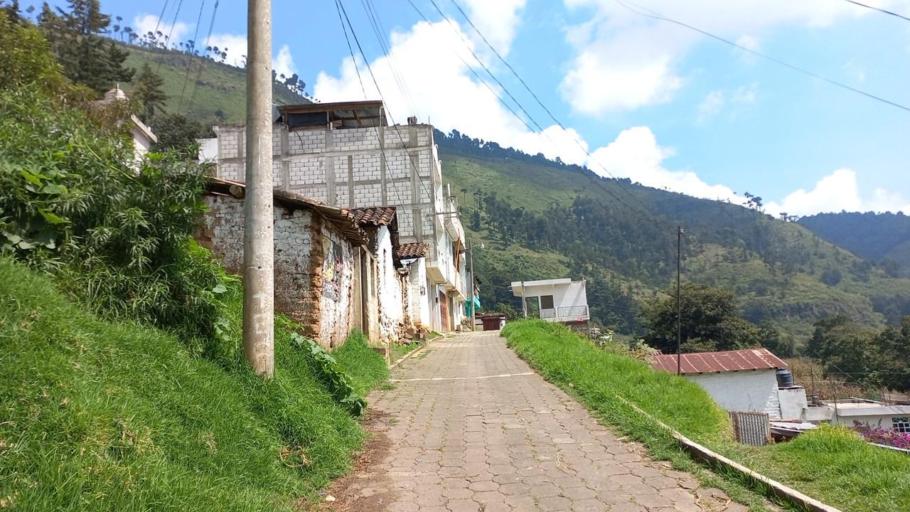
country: GT
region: Totonicapan
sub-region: Municipio de San Andres Xecul
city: San Andres Xecul
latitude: 14.9075
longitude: -91.4830
